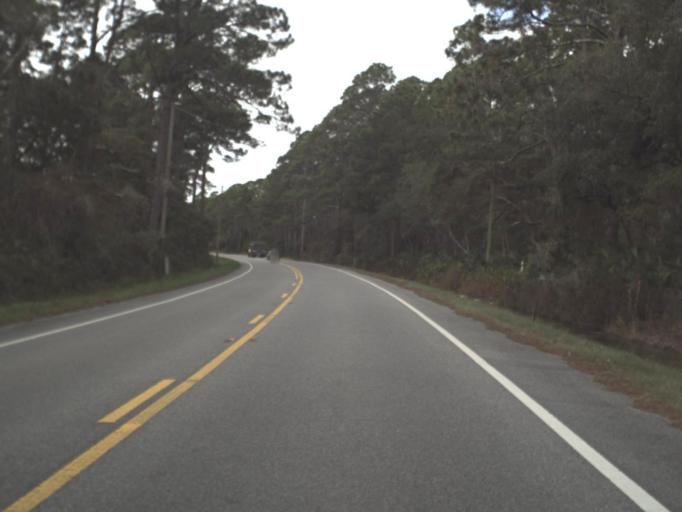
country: US
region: Florida
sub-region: Franklin County
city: Carrabelle
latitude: 29.8068
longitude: -84.7328
